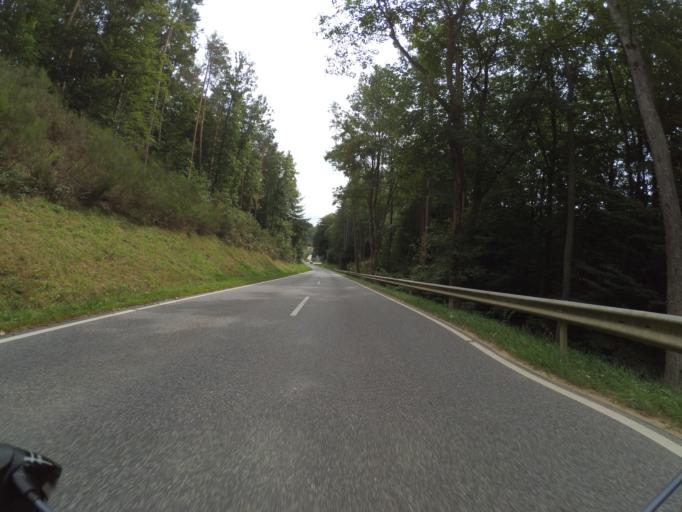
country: DE
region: Rheinland-Pfalz
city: Arenrath
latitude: 49.9454
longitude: 6.7409
